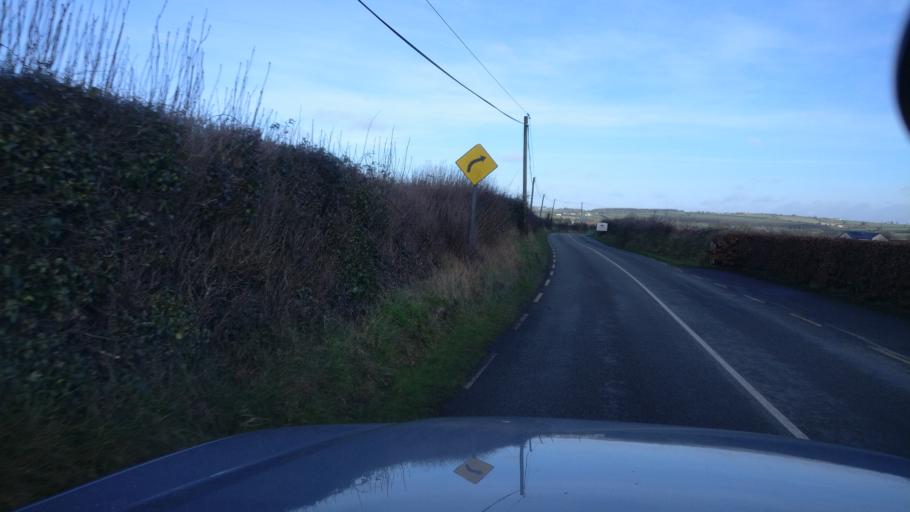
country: IE
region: Leinster
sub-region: Kilkenny
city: Castlecomer
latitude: 52.8558
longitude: -7.1702
